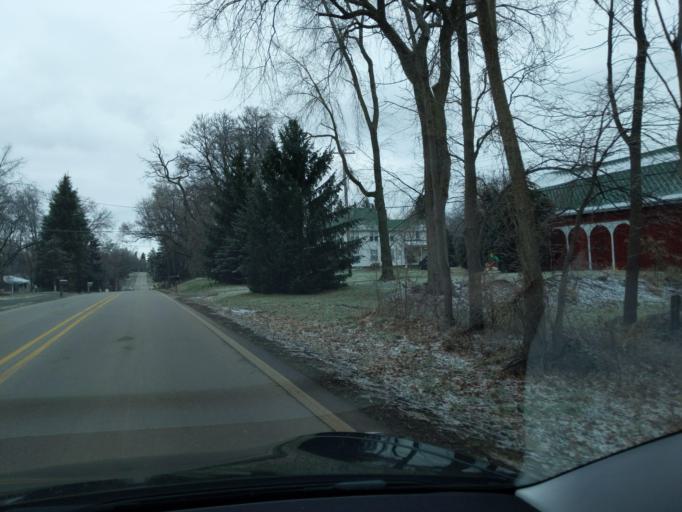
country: US
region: Michigan
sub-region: Jackson County
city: Spring Arbor
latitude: 42.1984
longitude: -84.5536
